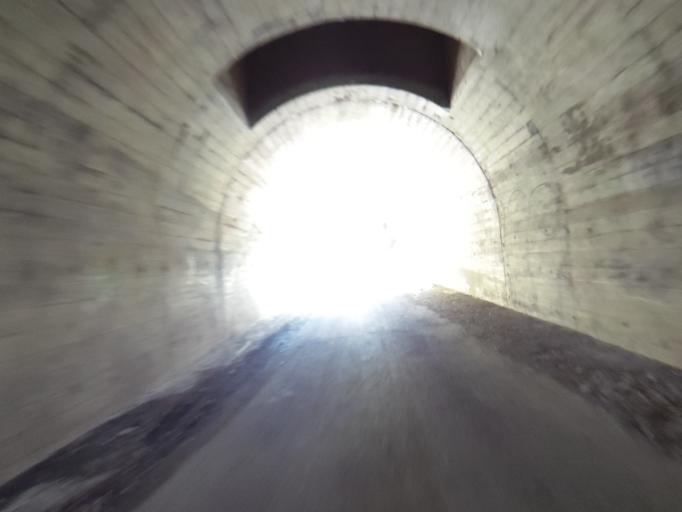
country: NL
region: Limburg
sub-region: Gemeente Kerkrade
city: Kerkrade
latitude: 50.8577
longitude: 6.0463
